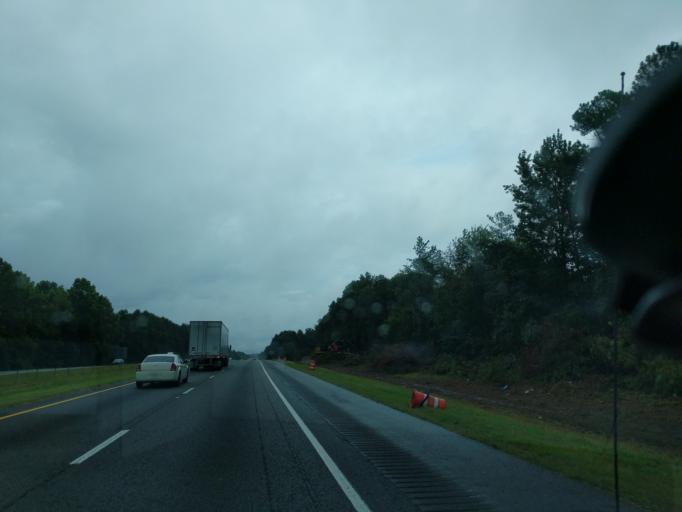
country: US
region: Georgia
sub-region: Banks County
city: Maysville
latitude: 34.1949
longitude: -83.5776
